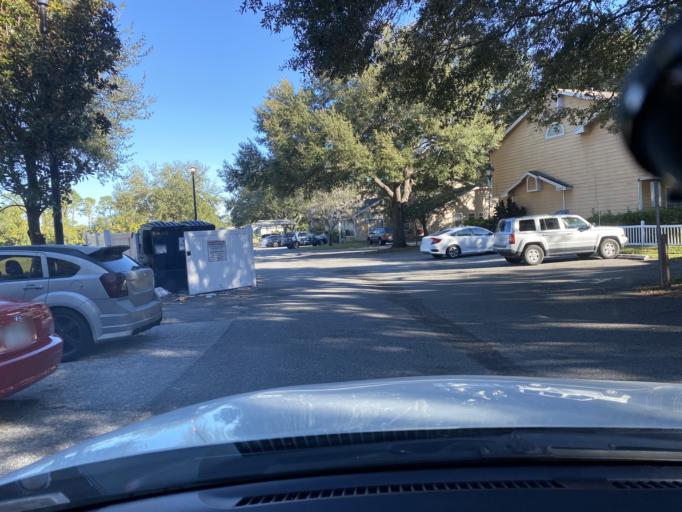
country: US
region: Florida
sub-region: Orange County
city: Conway
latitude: 28.5118
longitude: -81.3054
